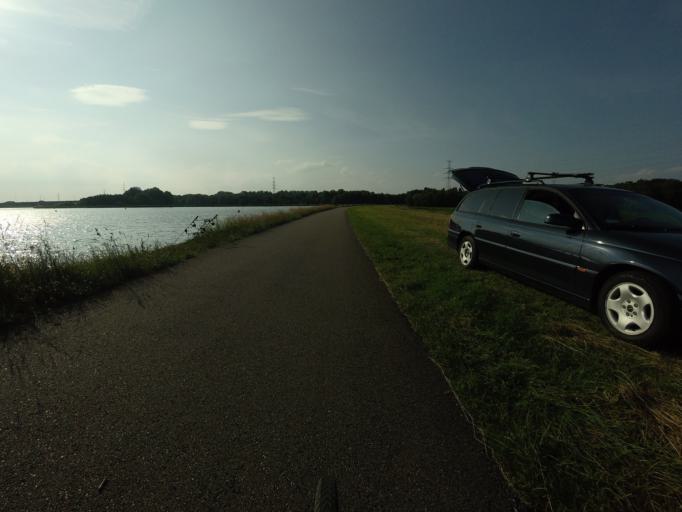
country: BE
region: Flanders
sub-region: Provincie Antwerpen
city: Zandhoven
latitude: 51.2030
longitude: 4.6186
